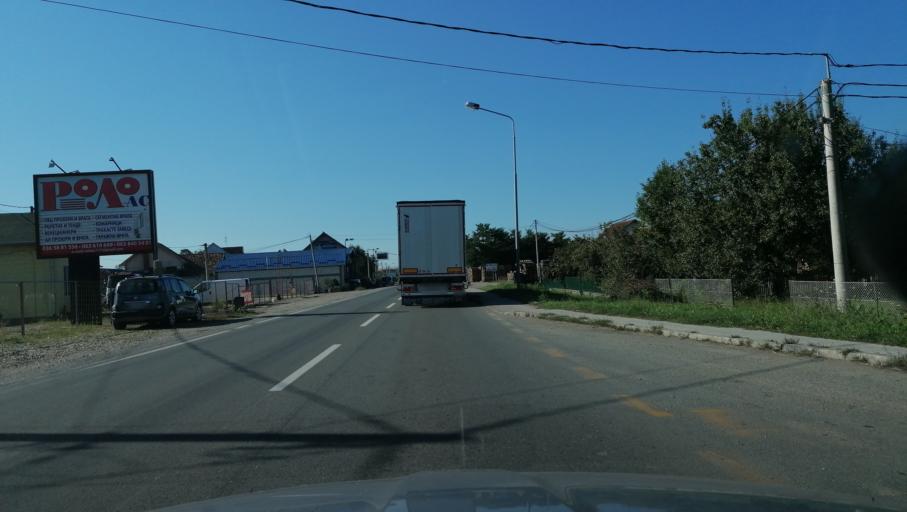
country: RS
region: Central Serbia
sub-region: Raski Okrug
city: Kraljevo
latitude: 43.7535
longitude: 20.6590
